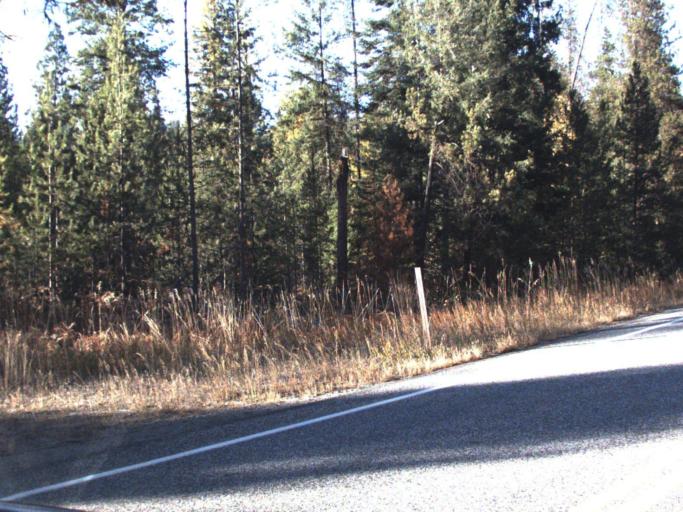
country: CA
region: British Columbia
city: Rossland
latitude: 48.9543
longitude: -117.7931
